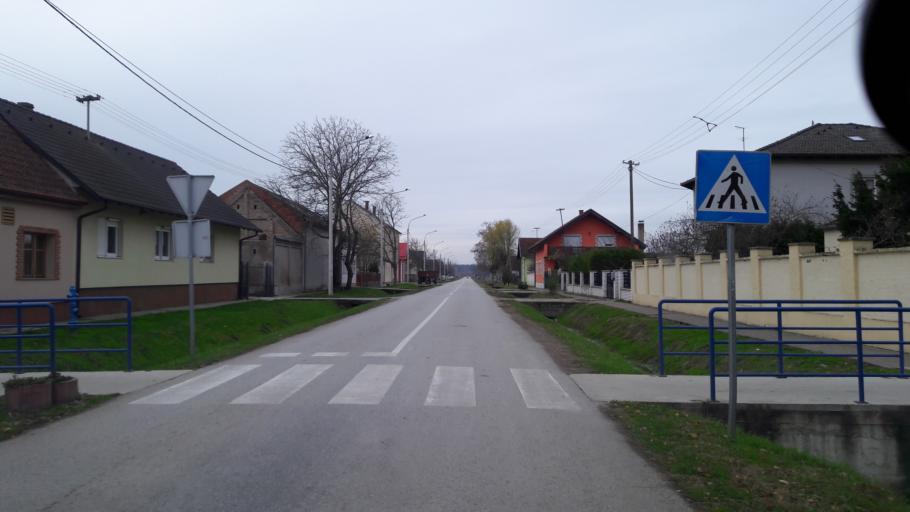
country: HR
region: Osjecko-Baranjska
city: Vladislavci
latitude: 45.4608
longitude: 18.5726
